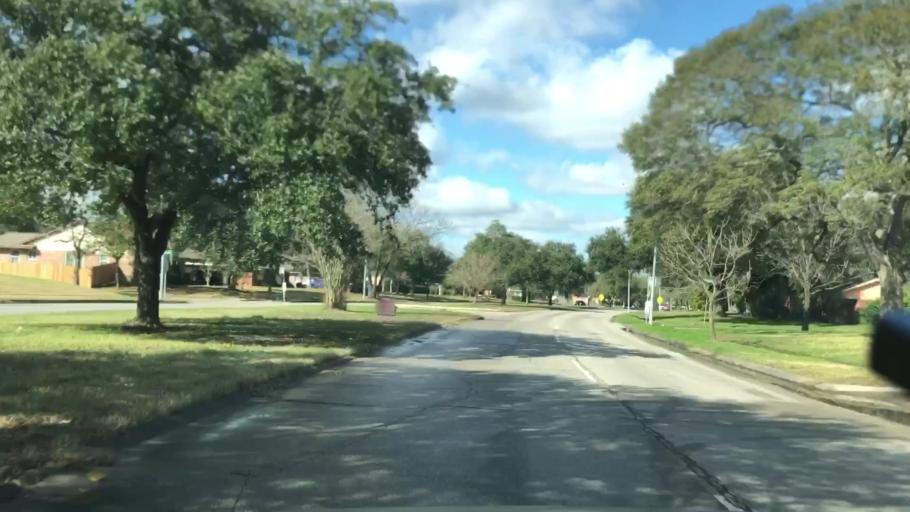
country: US
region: Texas
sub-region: Harris County
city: Bellaire
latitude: 29.6646
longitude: -95.4670
